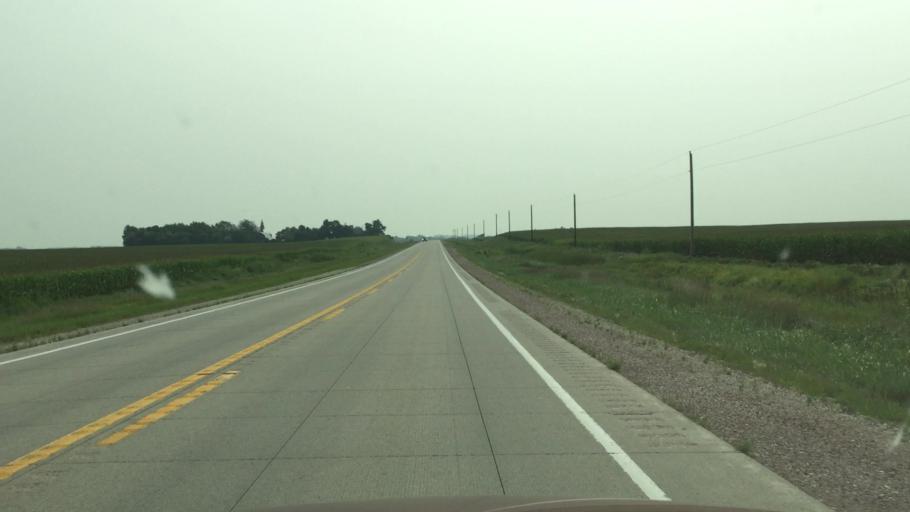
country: US
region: Iowa
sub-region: Osceola County
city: Sibley
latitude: 43.4328
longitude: -95.6322
